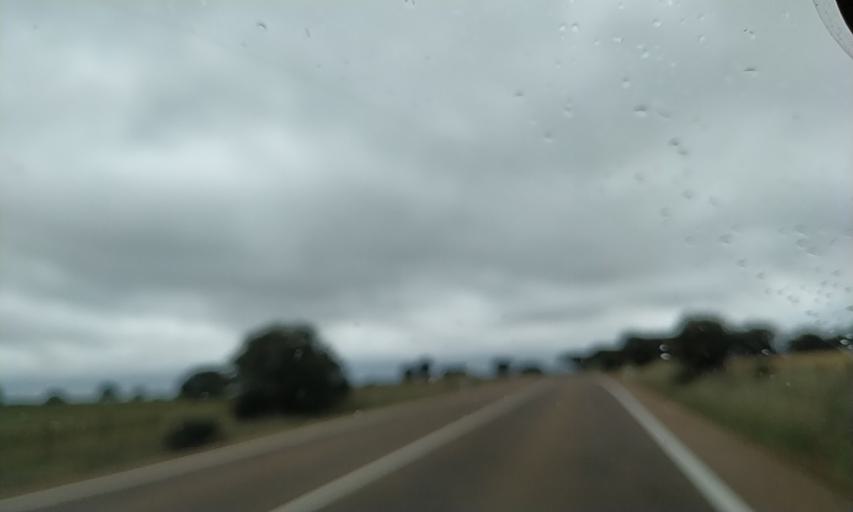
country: ES
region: Extremadura
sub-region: Provincia de Badajoz
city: Villar del Rey
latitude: 39.0275
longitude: -6.8393
